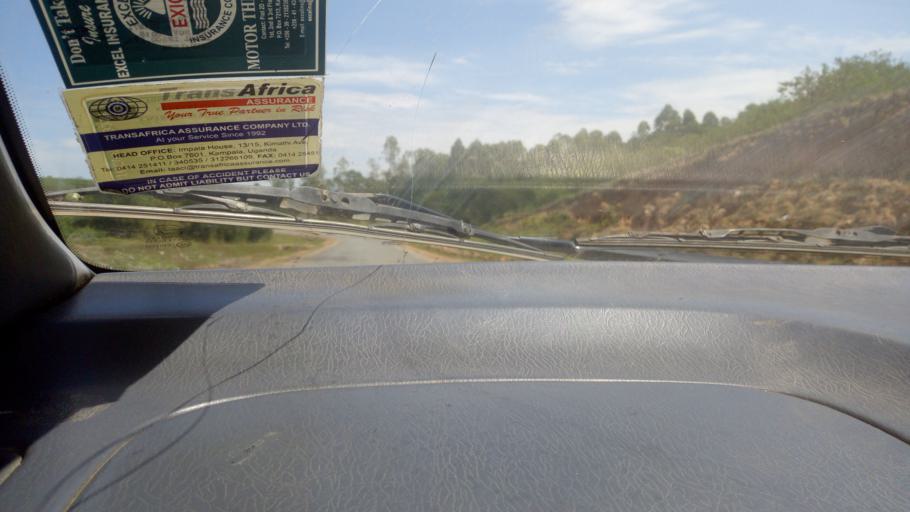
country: UG
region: Western Region
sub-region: Buhweju District
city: Buhweju
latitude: -0.2786
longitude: 30.5623
